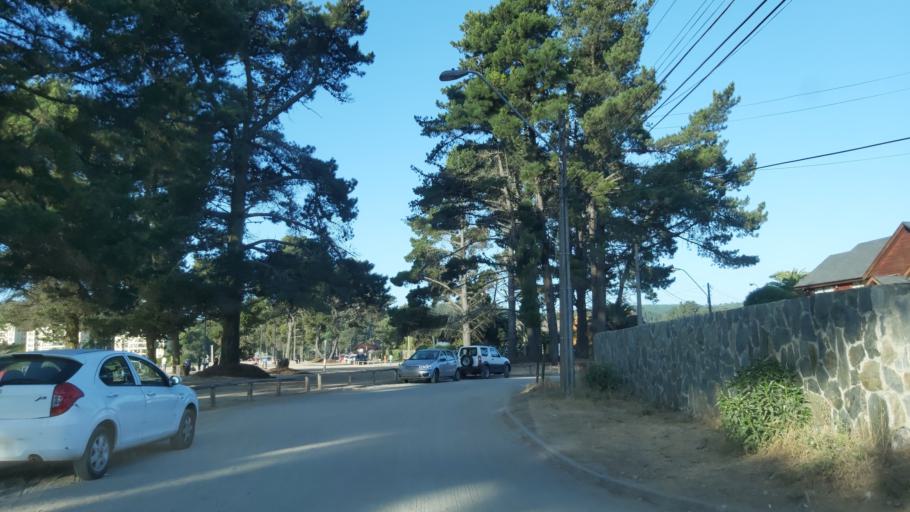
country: CL
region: Biobio
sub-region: Provincia de Concepcion
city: Tome
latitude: -36.5299
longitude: -72.9341
